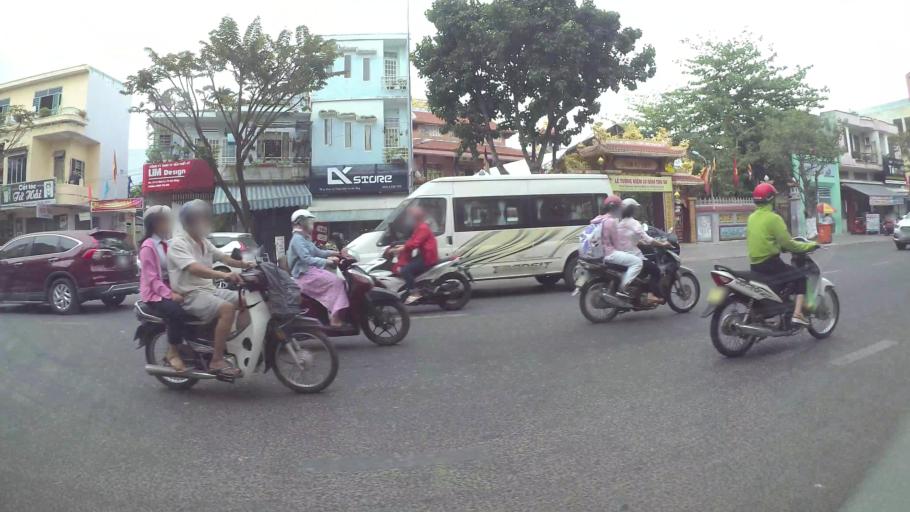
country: VN
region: Da Nang
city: Da Nang
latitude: 16.0565
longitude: 108.2118
